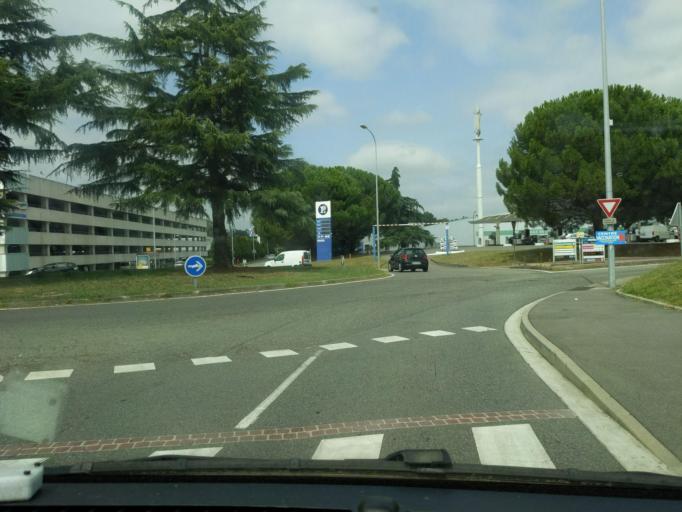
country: FR
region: Midi-Pyrenees
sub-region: Departement de la Haute-Garonne
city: Saint-Orens-de-Gameville
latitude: 43.5651
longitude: 1.5194
